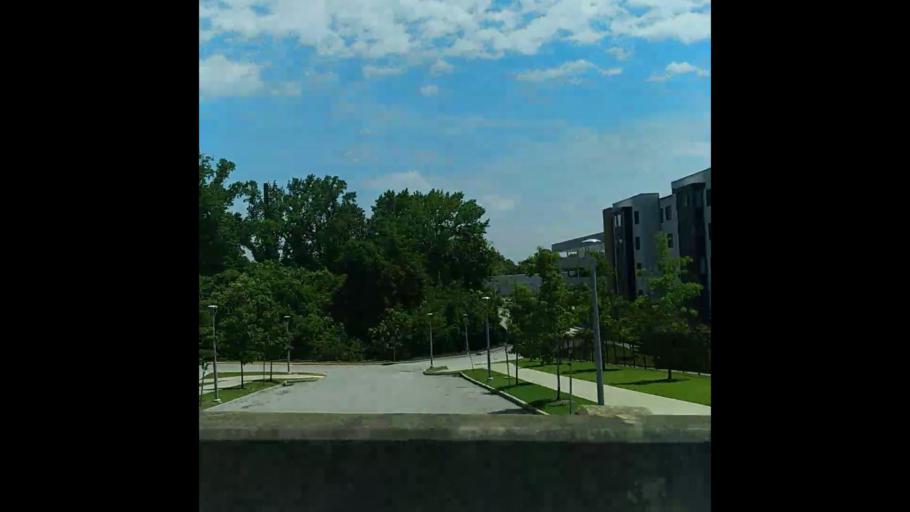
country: US
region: South Carolina
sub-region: Richland County
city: Columbia
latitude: 33.9901
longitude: -81.0393
